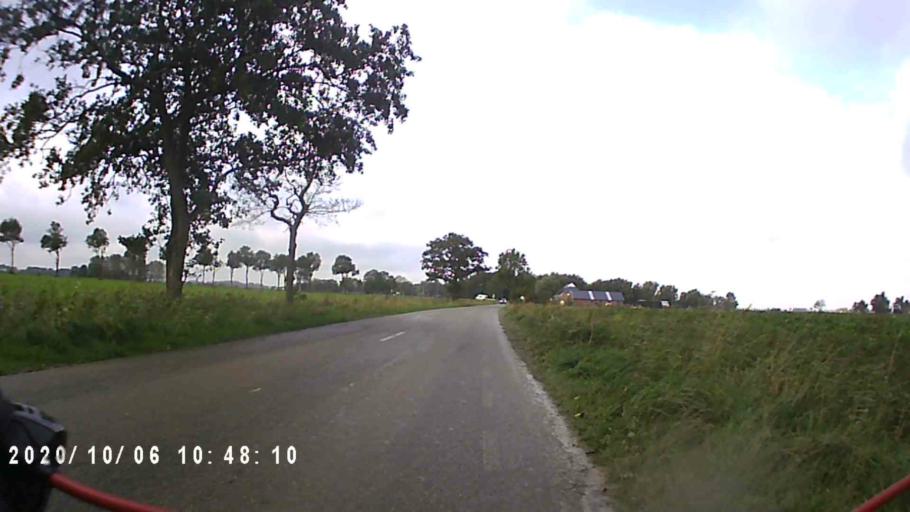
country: NL
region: Groningen
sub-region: Gemeente Zuidhorn
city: Oldehove
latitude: 53.3615
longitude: 6.4086
